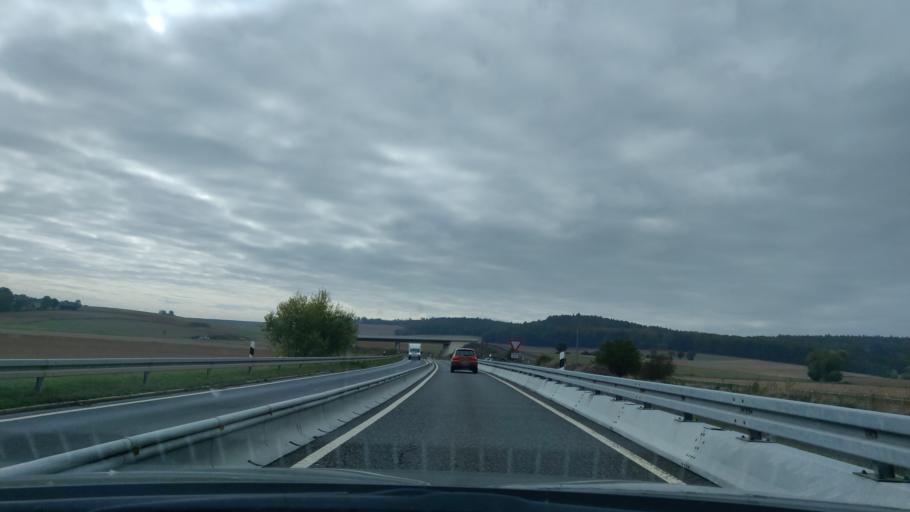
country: DE
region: Hesse
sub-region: Regierungsbezirk Kassel
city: Neuental
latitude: 51.0043
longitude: 9.2027
